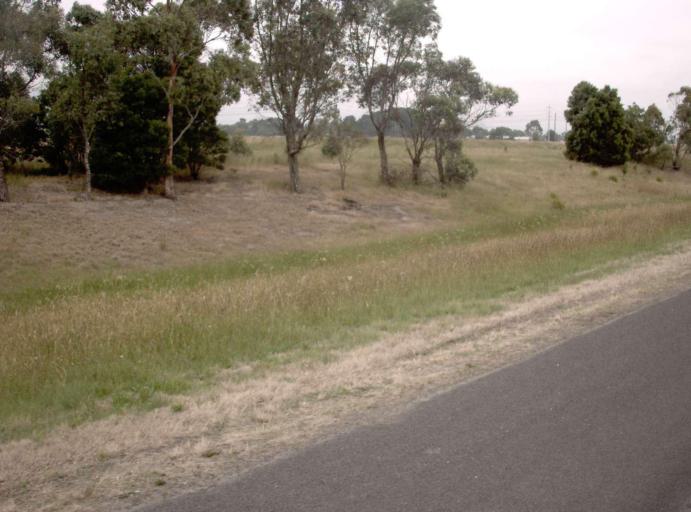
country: AU
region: Victoria
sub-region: Latrobe
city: Morwell
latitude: -38.2367
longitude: 146.4520
